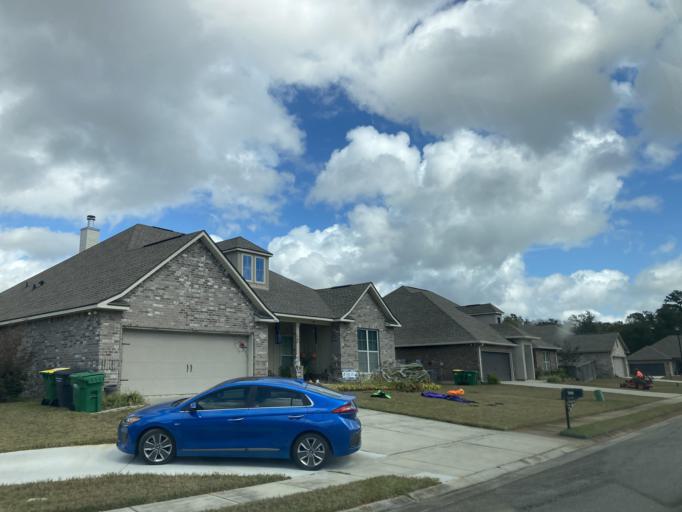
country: US
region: Mississippi
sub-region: Jackson County
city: Gulf Hills
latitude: 30.4503
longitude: -88.8250
